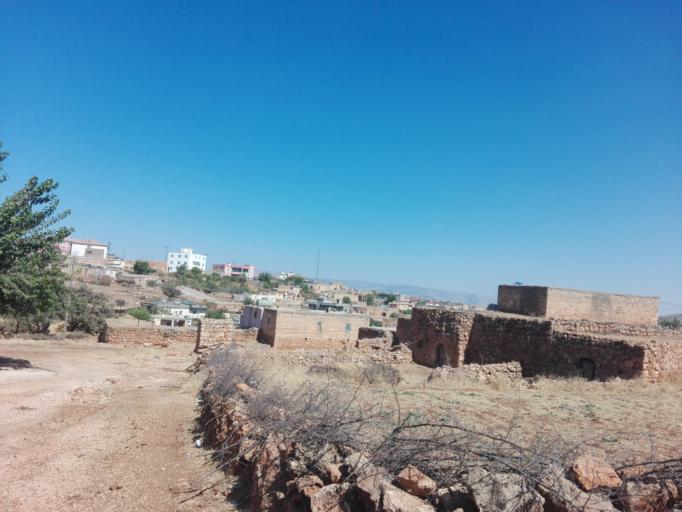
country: TR
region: Mardin
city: Kilavuz
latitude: 37.4808
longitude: 41.7781
